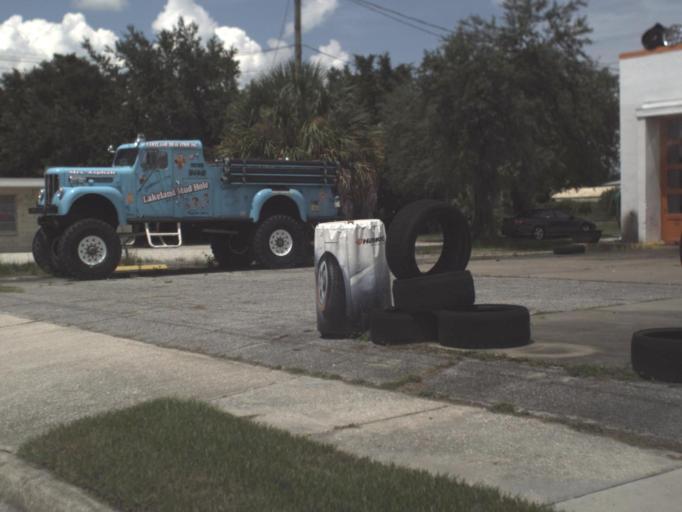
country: US
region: Florida
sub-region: Hillsborough County
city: Plant City
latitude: 28.0094
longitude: -82.1218
